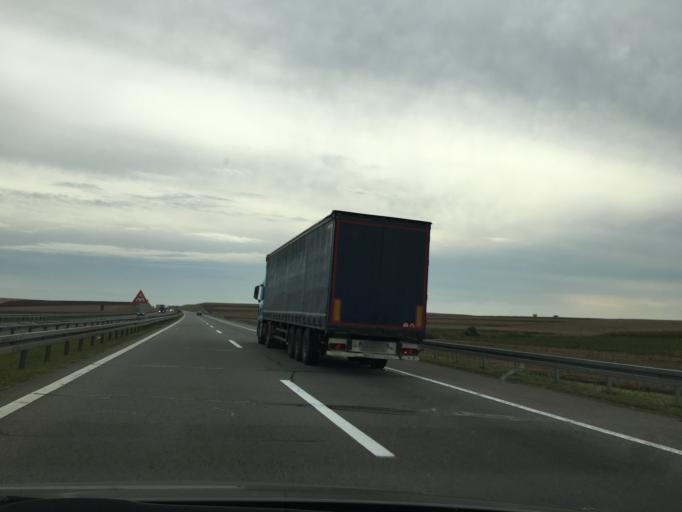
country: RS
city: Beska
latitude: 45.1314
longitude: 20.0896
